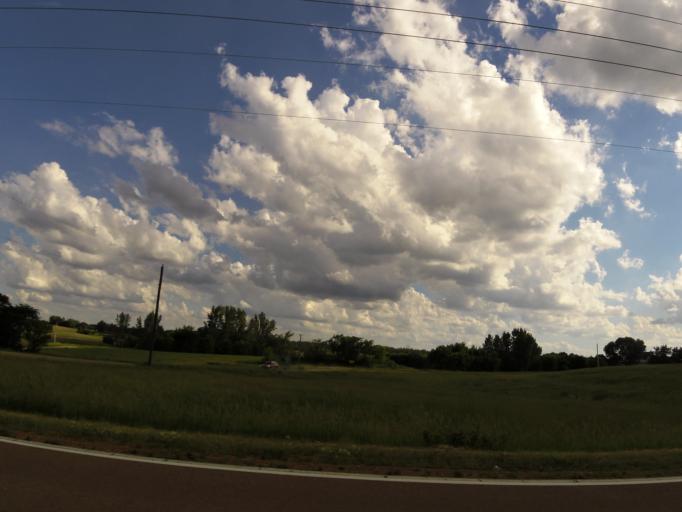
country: US
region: Minnesota
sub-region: Carver County
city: Waconia
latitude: 44.8201
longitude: -93.7351
